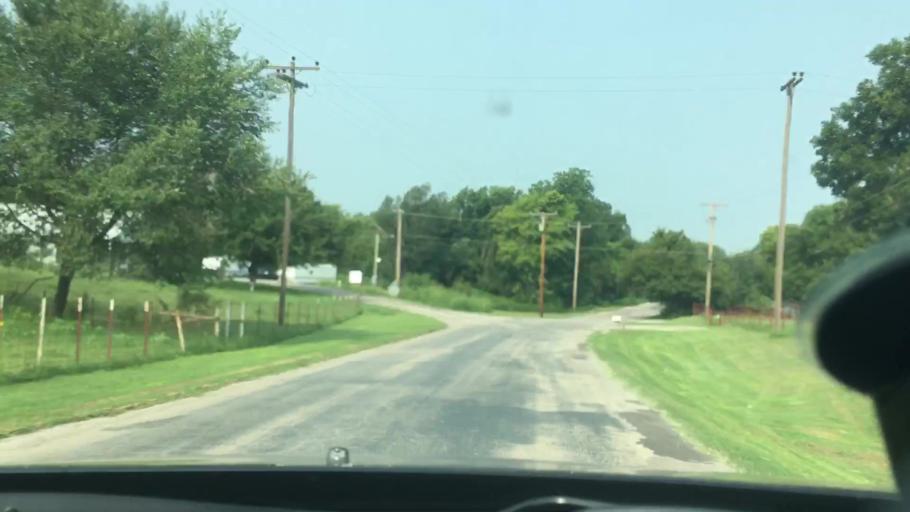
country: US
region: Oklahoma
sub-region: Garvin County
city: Lindsay
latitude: 34.8122
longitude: -97.6030
